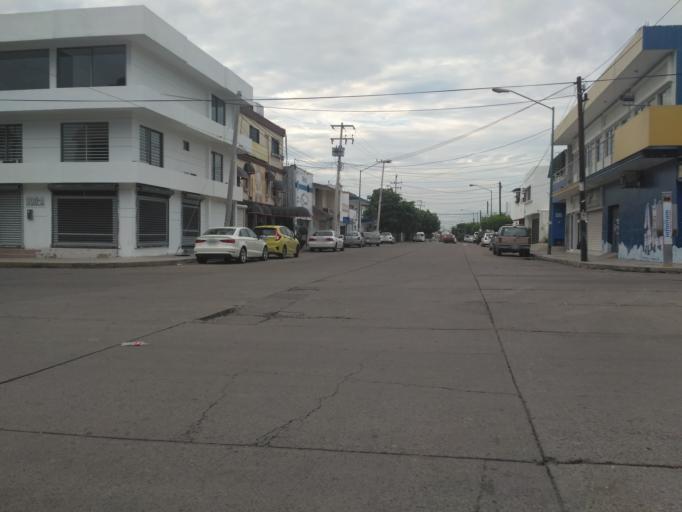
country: MX
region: Sinaloa
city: Culiacan
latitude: 24.7989
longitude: -107.3975
